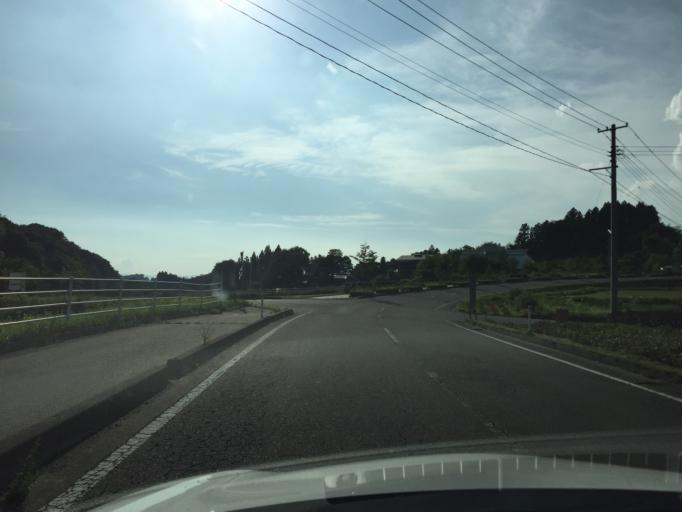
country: JP
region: Fukushima
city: Miharu
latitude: 37.4054
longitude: 140.5019
